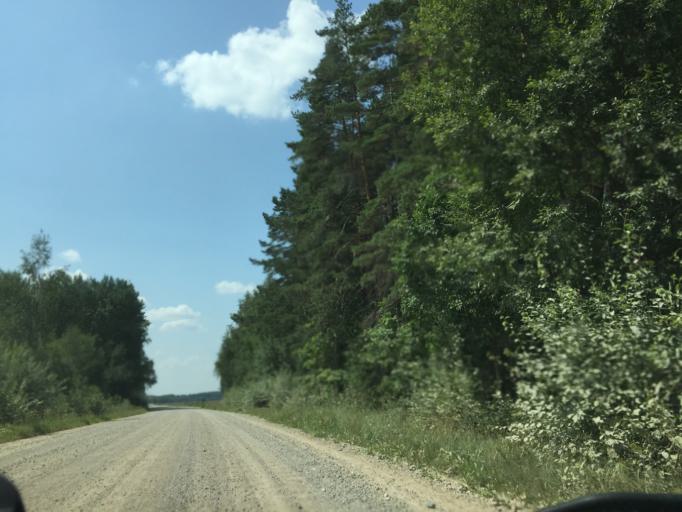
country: LT
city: Zagare
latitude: 56.3837
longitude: 23.2964
